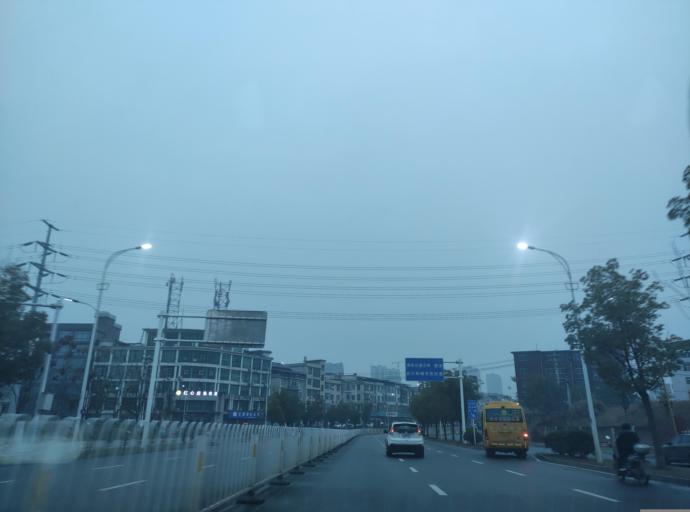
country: CN
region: Jiangxi Sheng
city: Pingxiang
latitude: 27.6691
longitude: 113.8711
